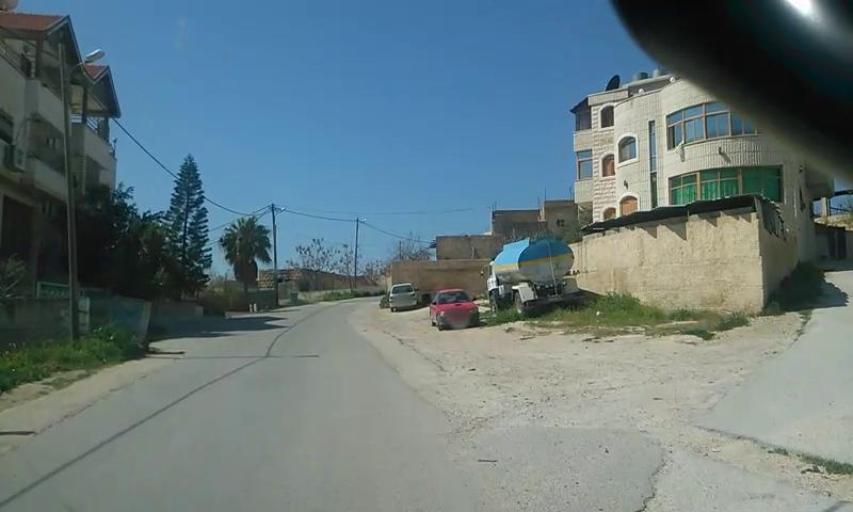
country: PS
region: West Bank
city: Al Majd
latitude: 31.4796
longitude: 34.9520
